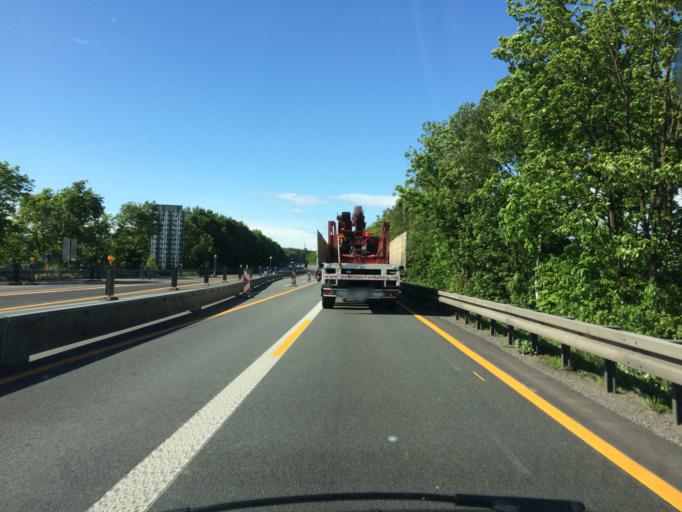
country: DE
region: North Rhine-Westphalia
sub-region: Regierungsbezirk Munster
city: Haltern
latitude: 51.7187
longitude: 7.1513
